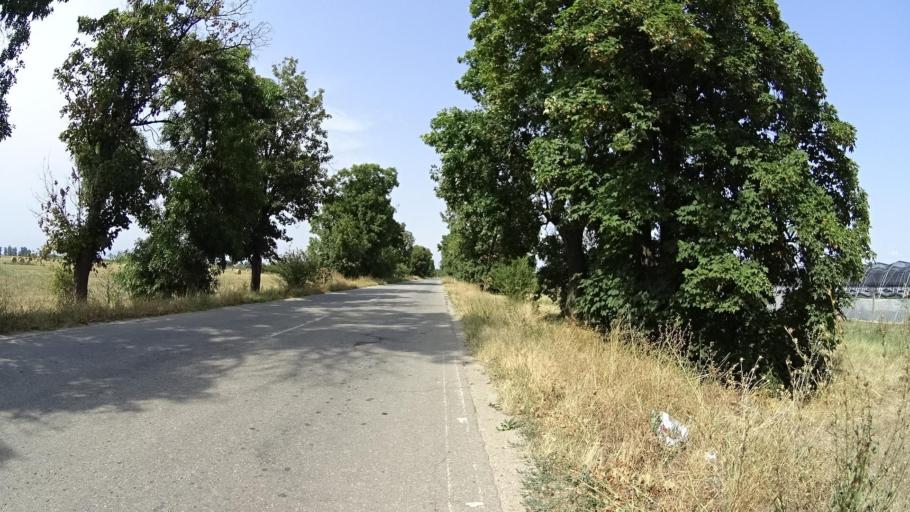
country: BG
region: Plovdiv
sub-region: Obshtina Kaloyanovo
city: Kaloyanovo
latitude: 42.2590
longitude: 24.8000
